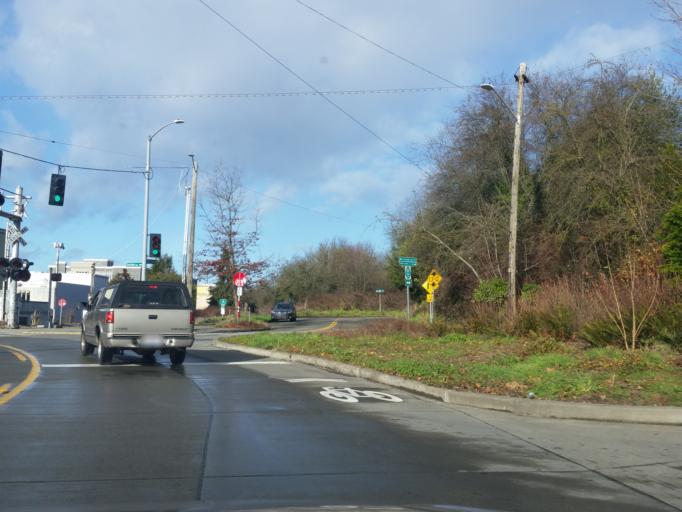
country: US
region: Washington
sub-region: King County
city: Seattle
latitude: 47.6720
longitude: -122.4053
